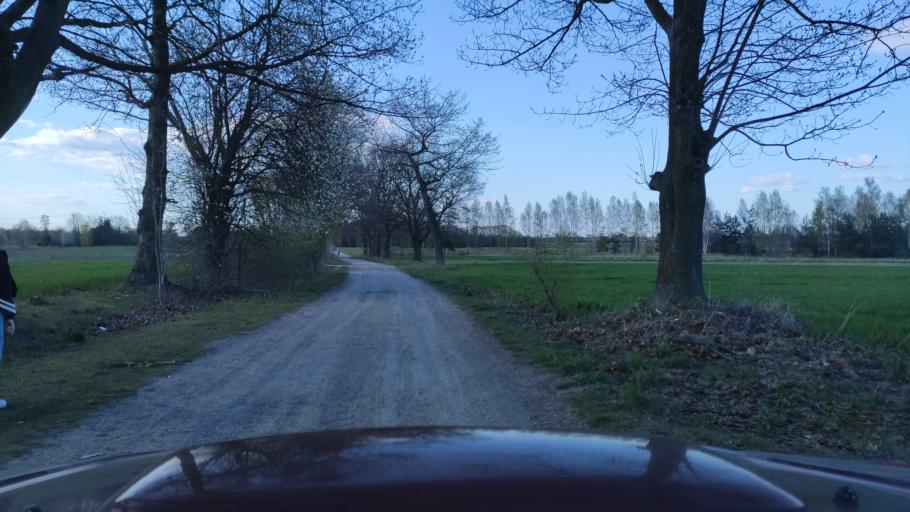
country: PL
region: Masovian Voivodeship
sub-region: Powiat zwolenski
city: Zwolen
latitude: 51.3648
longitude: 21.5757
